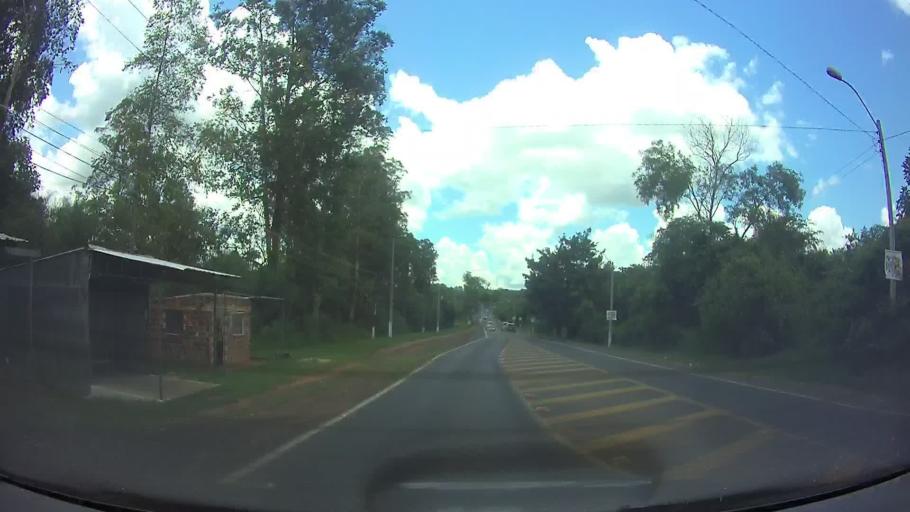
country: PY
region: Central
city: Capiata
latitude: -25.3493
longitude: -57.4175
